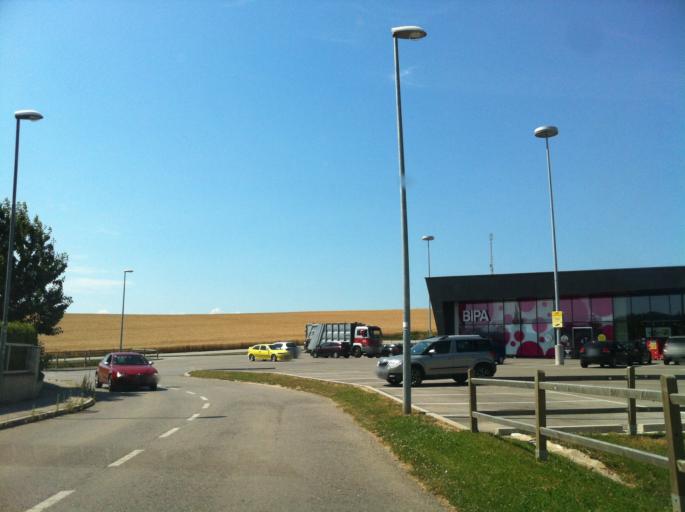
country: AT
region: Lower Austria
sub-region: Politischer Bezirk Tulln
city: Sieghartskirchen
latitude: 48.2564
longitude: 16.0077
